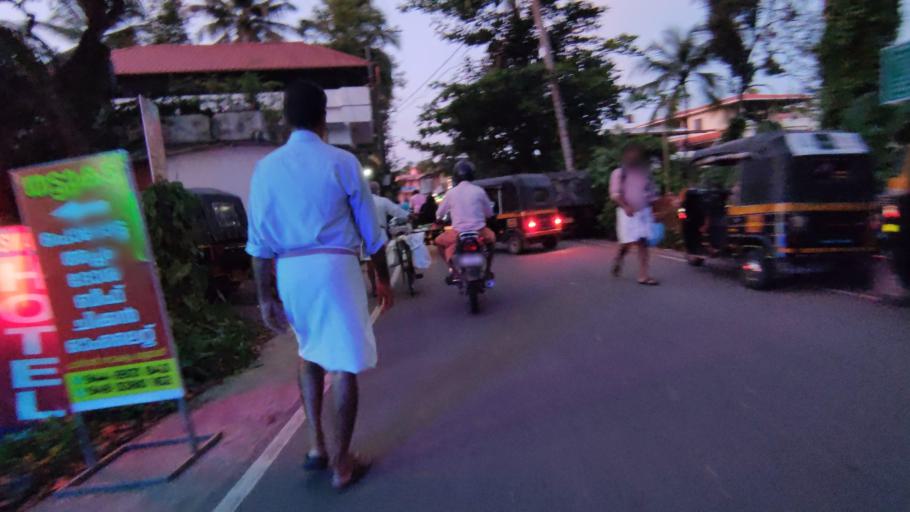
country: IN
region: Kerala
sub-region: Kottayam
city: Kottayam
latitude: 9.5905
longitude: 76.4371
